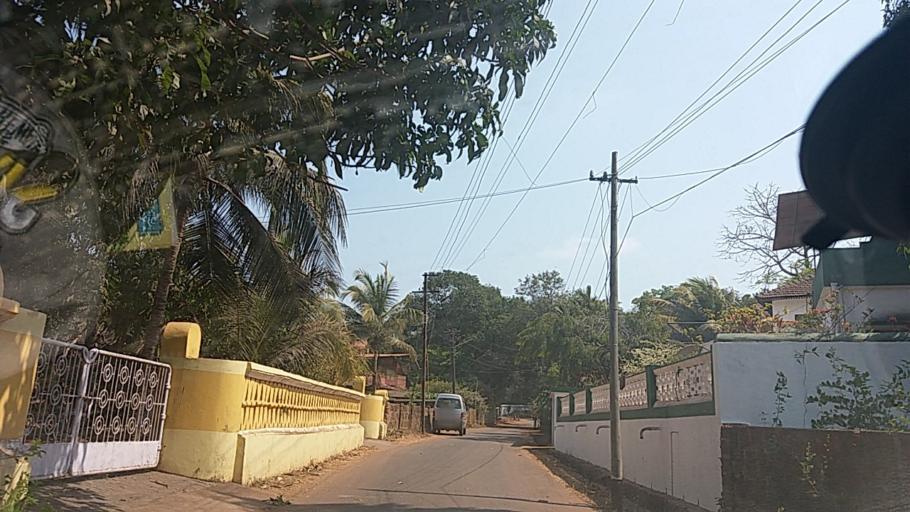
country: IN
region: Goa
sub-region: North Goa
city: Saligao
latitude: 15.5390
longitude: 73.7845
